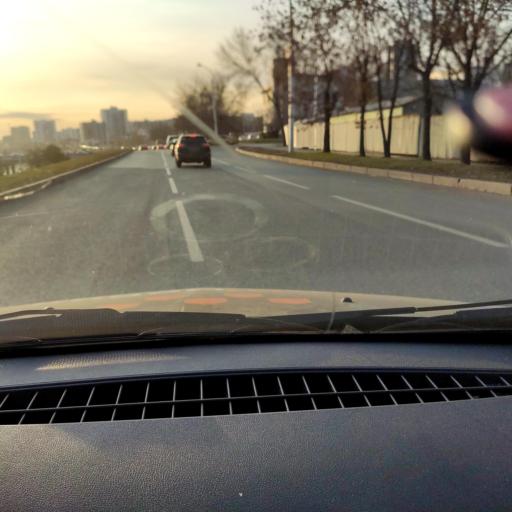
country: RU
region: Bashkortostan
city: Ufa
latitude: 54.7200
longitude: 55.9713
